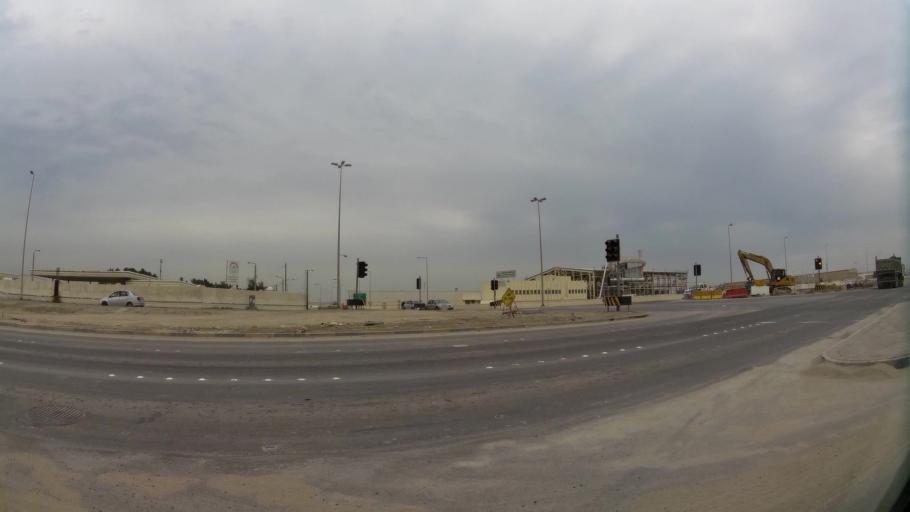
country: BH
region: Northern
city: Sitrah
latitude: 26.1773
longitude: 50.6097
